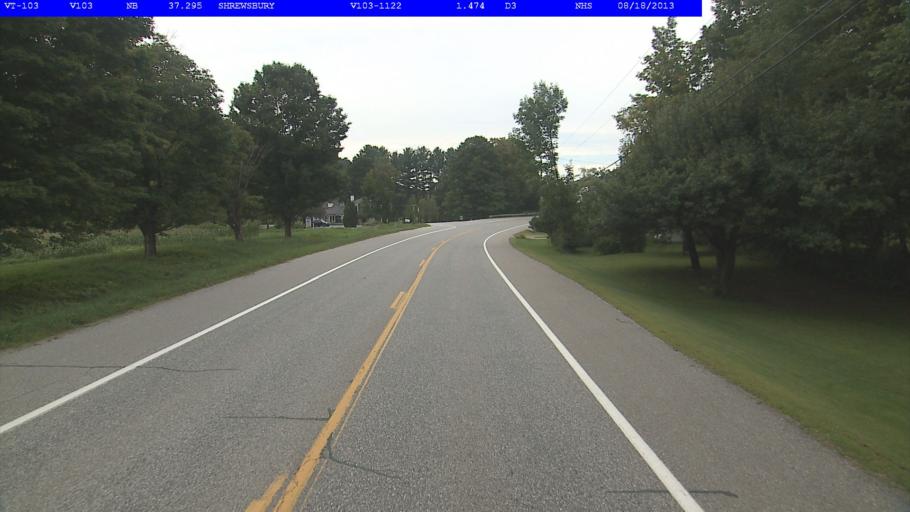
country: US
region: Vermont
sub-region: Rutland County
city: Rutland
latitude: 43.4961
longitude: -72.8930
